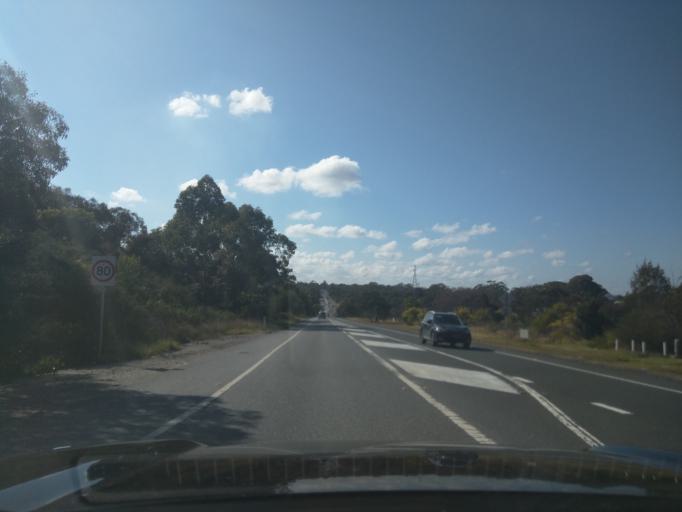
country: AU
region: New South Wales
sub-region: Sutherland Shire
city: Engadine
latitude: -34.0482
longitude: 150.9814
